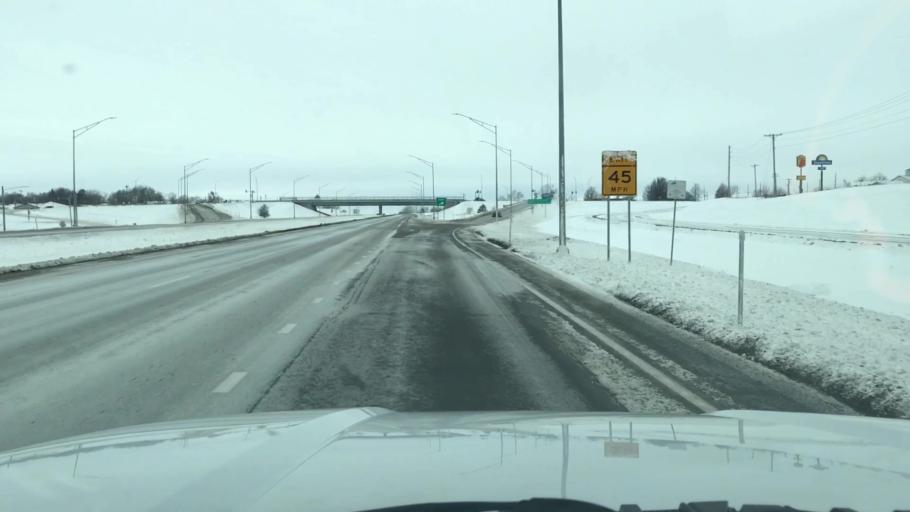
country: US
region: Missouri
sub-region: Clinton County
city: Cameron
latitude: 39.7544
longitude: -94.2290
